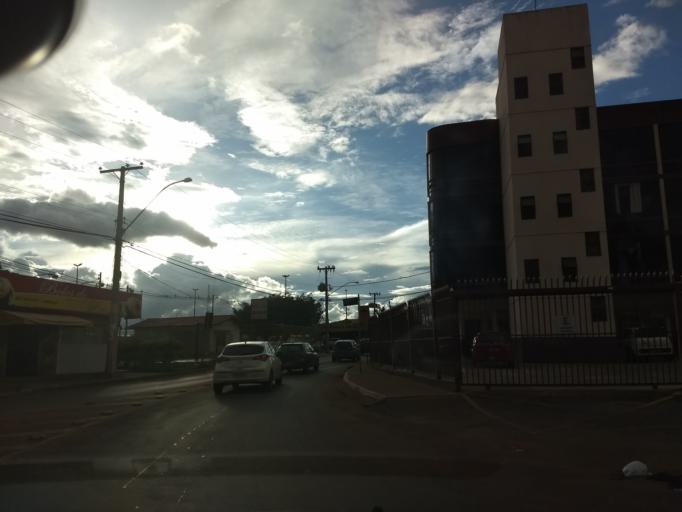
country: BR
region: Federal District
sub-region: Brasilia
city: Brasilia
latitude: -15.8107
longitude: -47.9873
